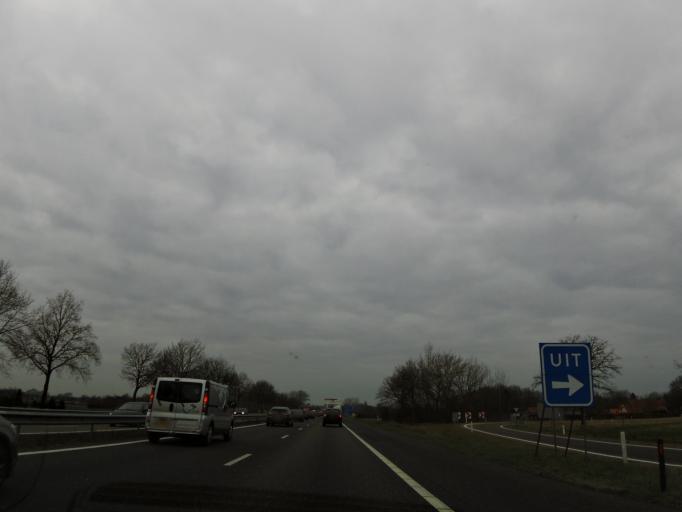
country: NL
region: North Brabant
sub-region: Gemeente Cranendonck
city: Cranendonck
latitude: 51.3398
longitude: 5.5638
